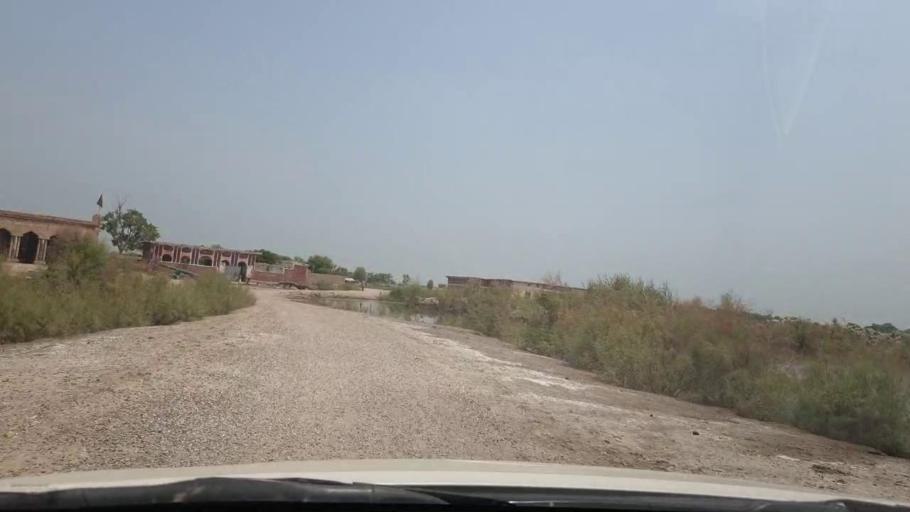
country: PK
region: Sindh
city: Rustam jo Goth
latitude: 28.0271
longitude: 68.7887
